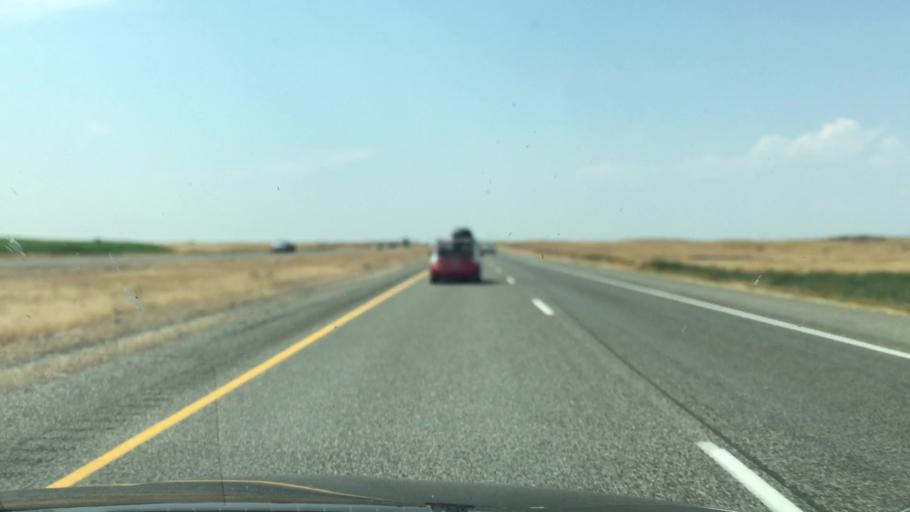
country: US
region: Idaho
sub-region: Gooding County
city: Wendell
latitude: 42.8144
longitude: -114.7798
